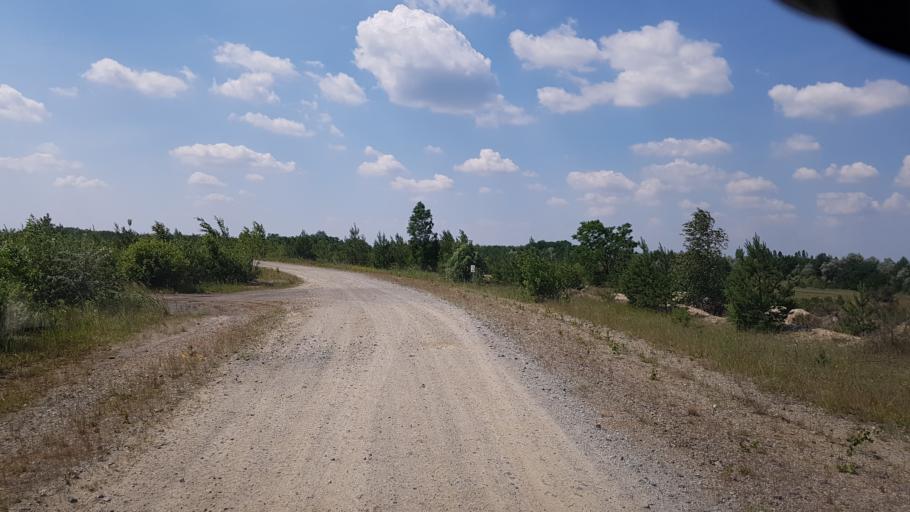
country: DE
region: Brandenburg
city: Sallgast
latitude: 51.5573
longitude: 13.7871
